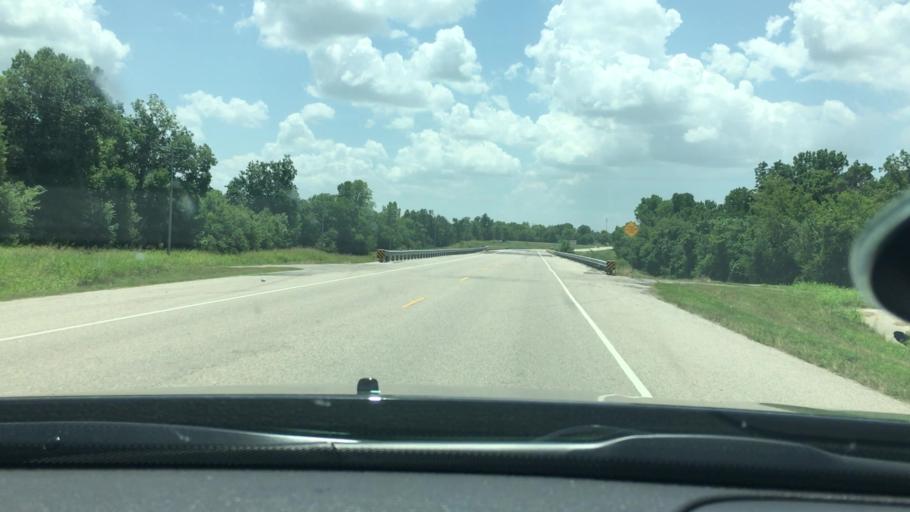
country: US
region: Oklahoma
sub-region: Johnston County
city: Tishomingo
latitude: 34.4565
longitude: -96.6359
